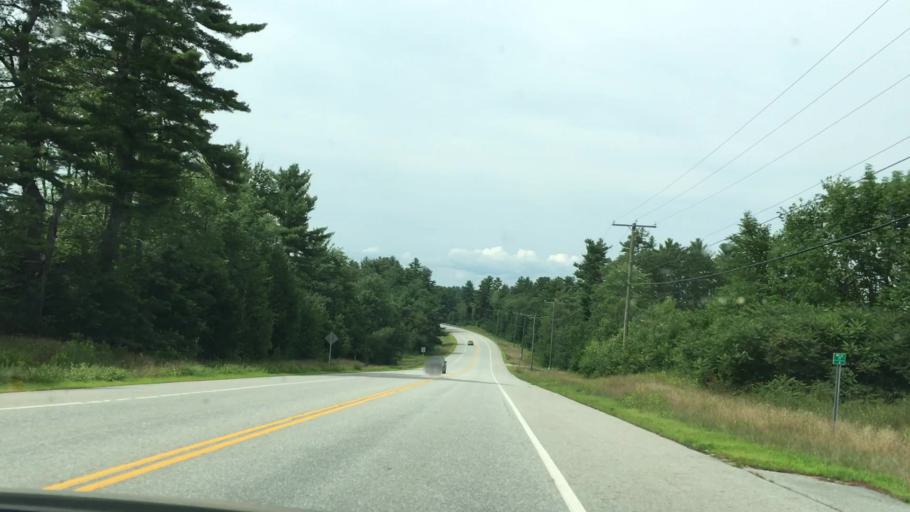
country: US
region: New Hampshire
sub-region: Hillsborough County
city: Peterborough
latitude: 42.9160
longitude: -71.9396
